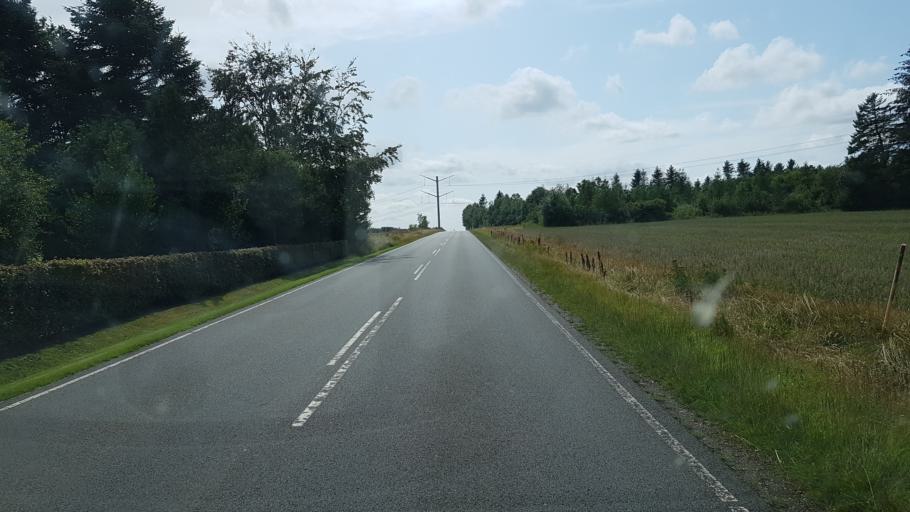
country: DK
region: South Denmark
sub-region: Vejen Kommune
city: Vejen
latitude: 55.5827
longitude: 9.1600
